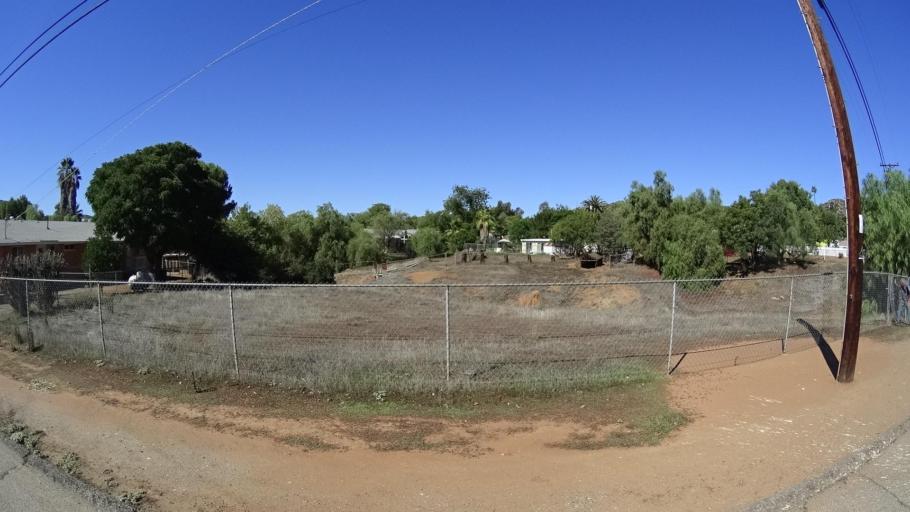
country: US
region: California
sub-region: San Diego County
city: Harbison Canyon
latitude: 32.8658
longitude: -116.8209
